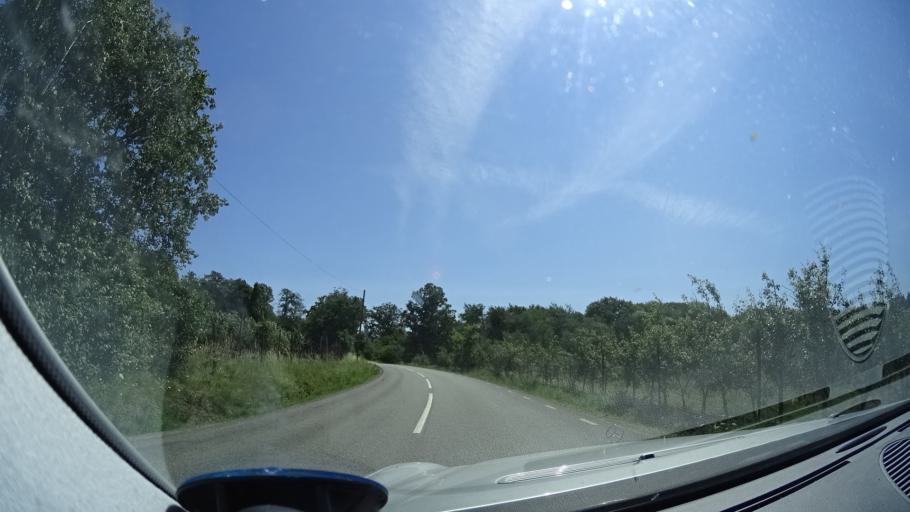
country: SE
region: Skane
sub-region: Kristianstads Kommun
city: Degeberga
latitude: 55.8925
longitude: 14.0031
